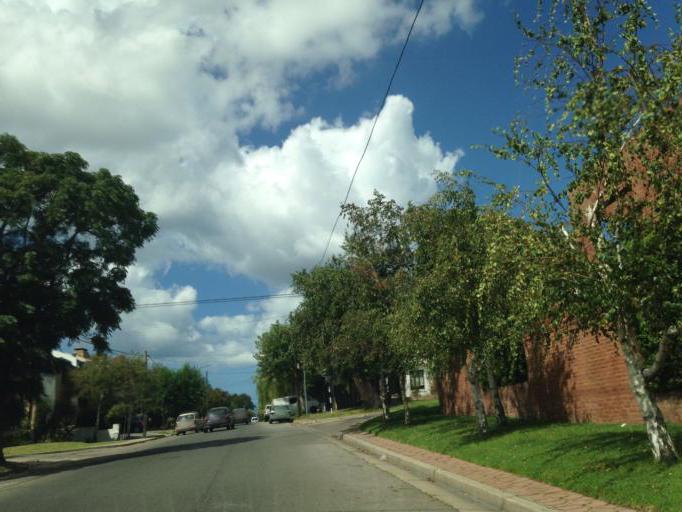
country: AR
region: Buenos Aires
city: Mar del Plata
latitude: -38.0211
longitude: -57.5552
